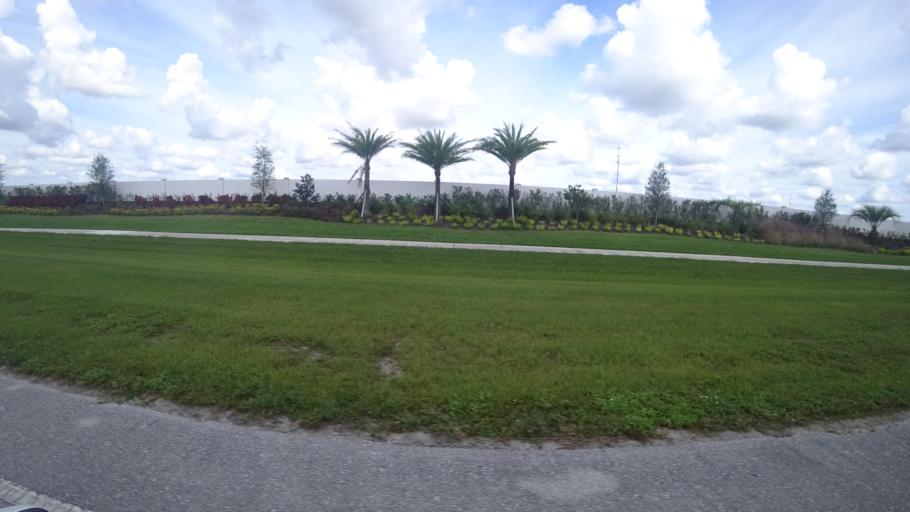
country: US
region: Florida
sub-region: Sarasota County
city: The Meadows
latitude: 27.3867
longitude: -82.3554
